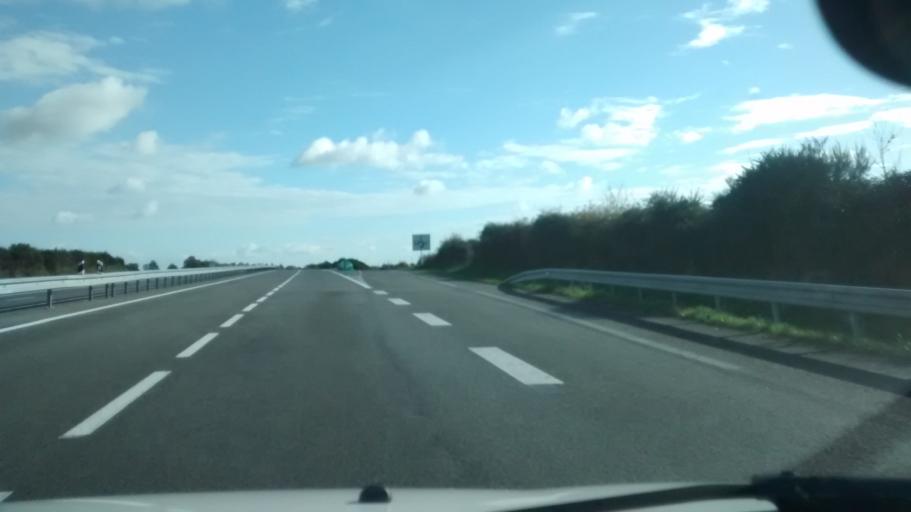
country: FR
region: Pays de la Loire
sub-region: Departement de Maine-et-Loire
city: Pouance
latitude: 47.7305
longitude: -1.1126
